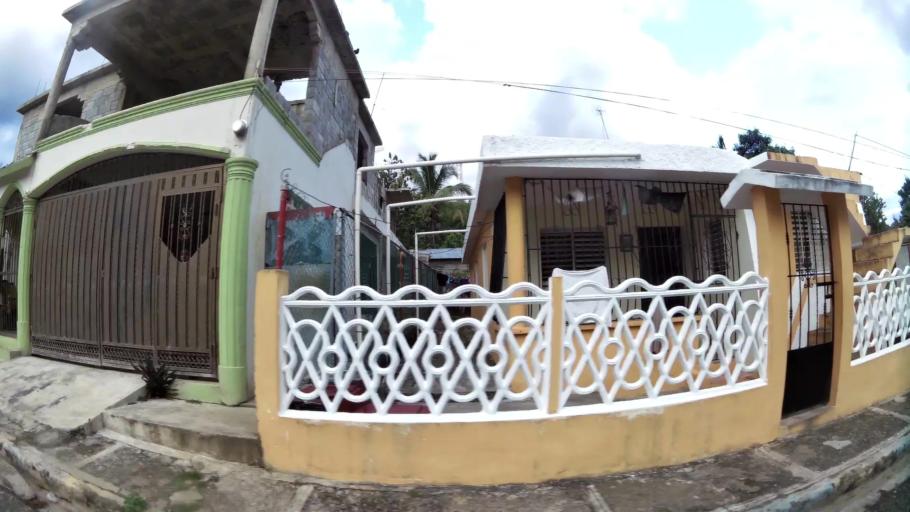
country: DO
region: San Cristobal
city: Villa Altagracia
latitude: 18.6696
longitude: -70.1660
